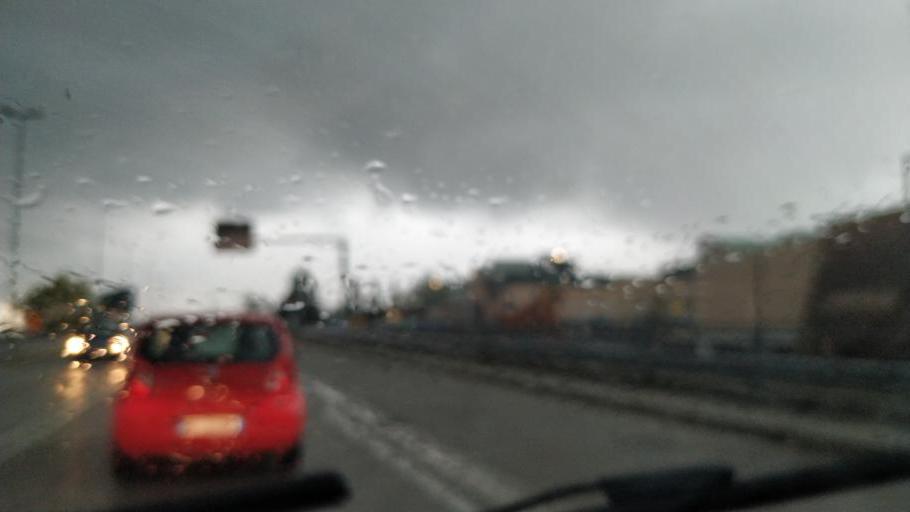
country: IT
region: Emilia-Romagna
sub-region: Provincia di Ferrara
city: Pontegradella
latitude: 44.8454
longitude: 11.6501
